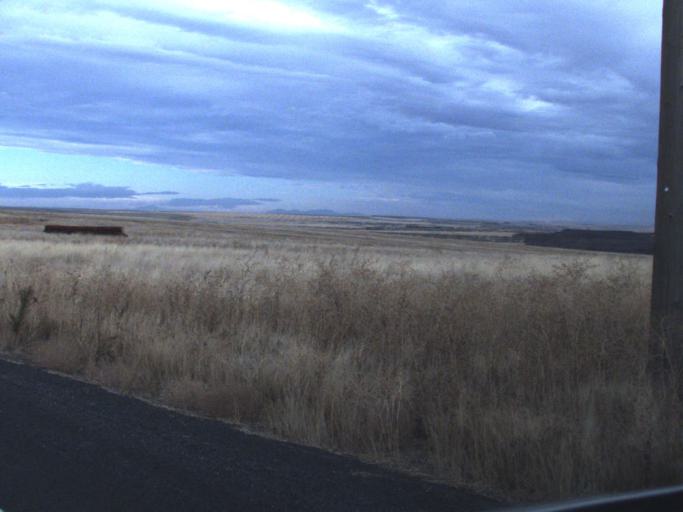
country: US
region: Washington
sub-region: Adams County
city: Ritzville
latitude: 47.4494
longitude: -118.7408
